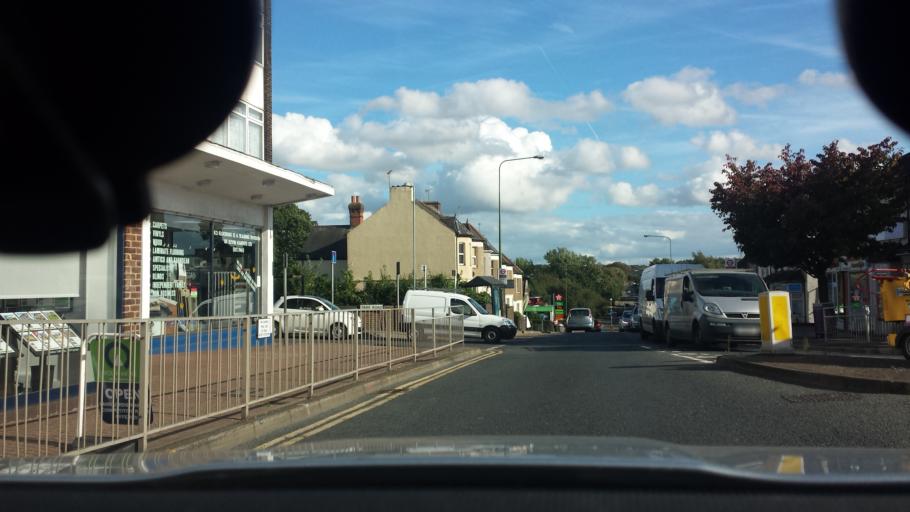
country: GB
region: England
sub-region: Kent
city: Swanley
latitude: 51.3949
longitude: 0.1786
